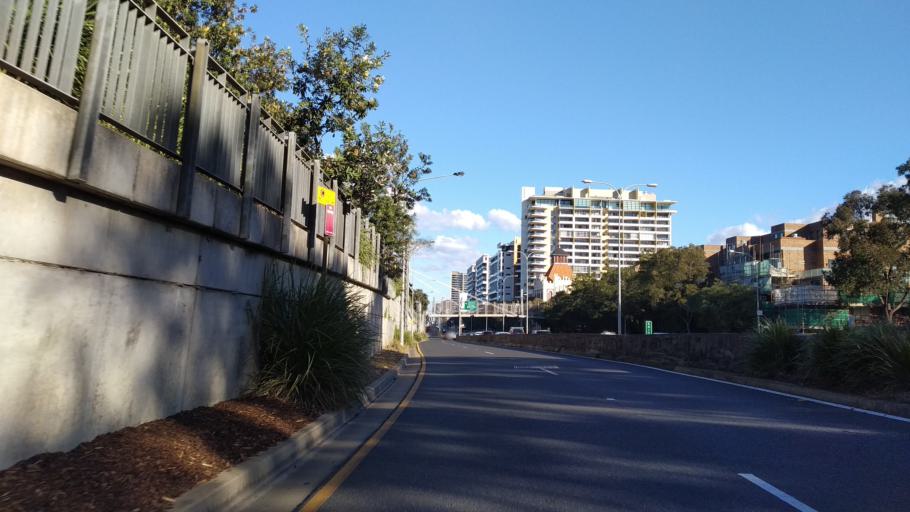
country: AU
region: New South Wales
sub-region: City of Sydney
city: Redfern
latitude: -33.8949
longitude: 151.2165
